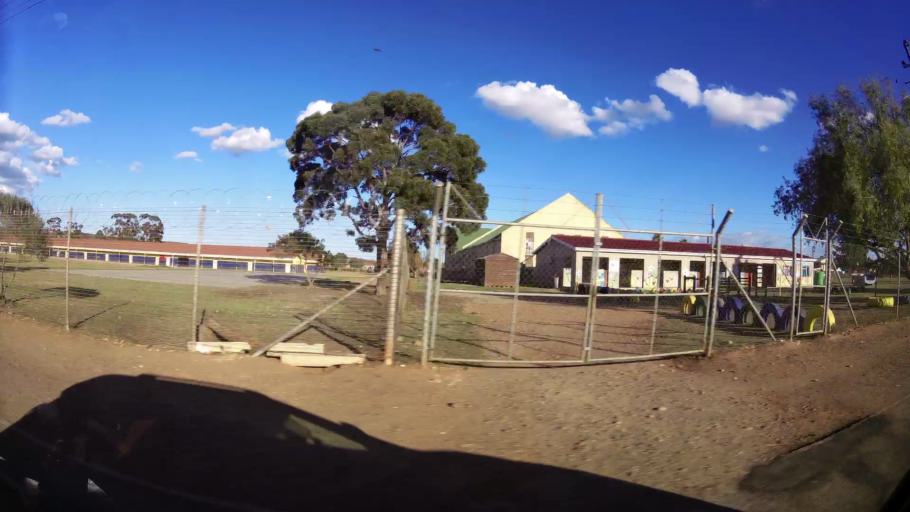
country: ZA
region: Western Cape
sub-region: Eden District Municipality
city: Riversdale
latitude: -34.1028
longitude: 20.9617
